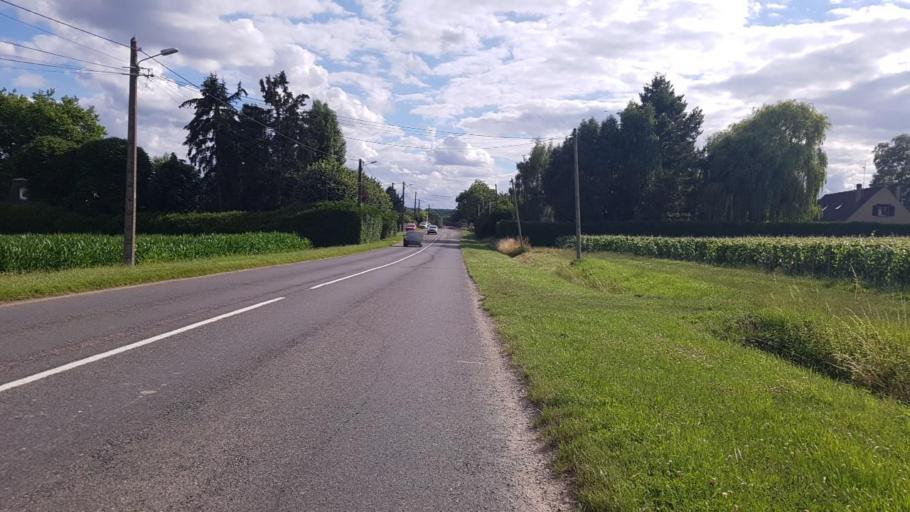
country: FR
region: Picardie
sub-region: Departement de l'Aisne
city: Brasles
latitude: 49.0515
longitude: 3.4691
